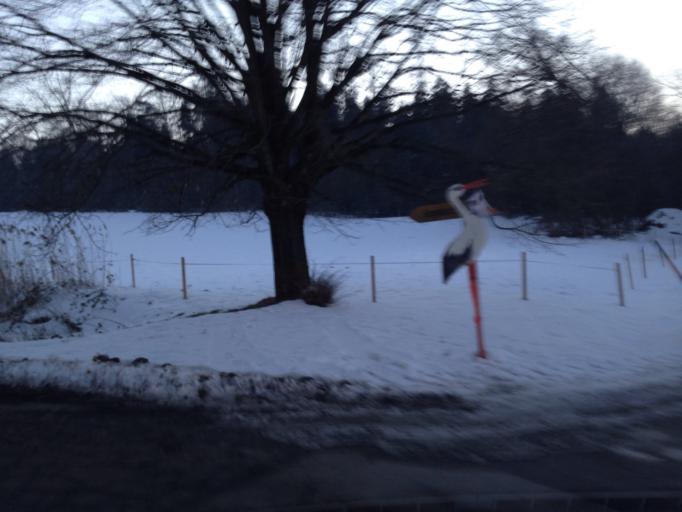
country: DE
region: Bavaria
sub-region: Upper Bavaria
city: Taching am See
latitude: 47.9775
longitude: 12.7213
